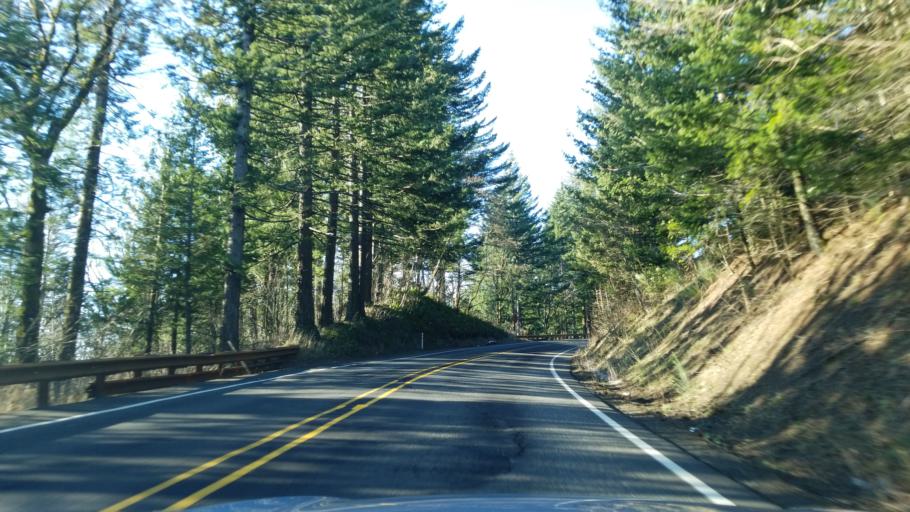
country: US
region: Washington
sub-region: Clark County
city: Washougal
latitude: 45.5884
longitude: -122.1656
